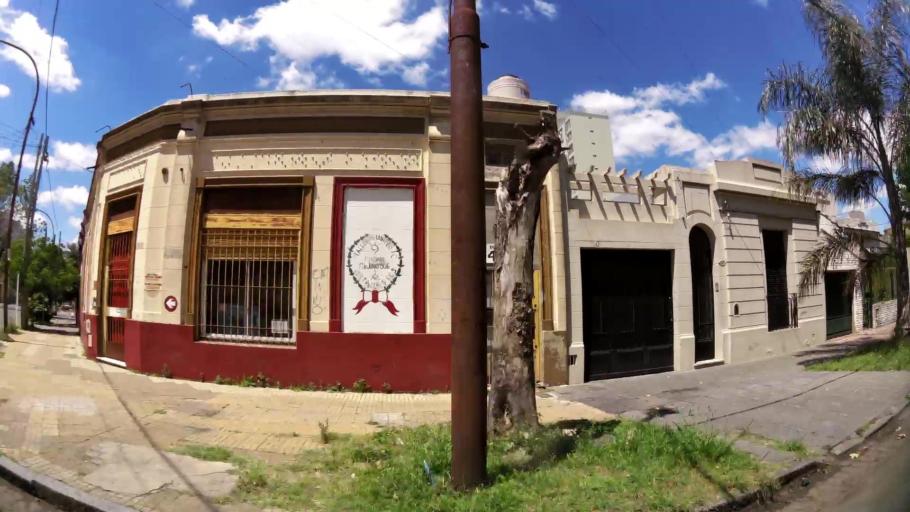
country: AR
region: Buenos Aires
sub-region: Partido de Lanus
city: Lanus
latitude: -34.7309
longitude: -58.3993
